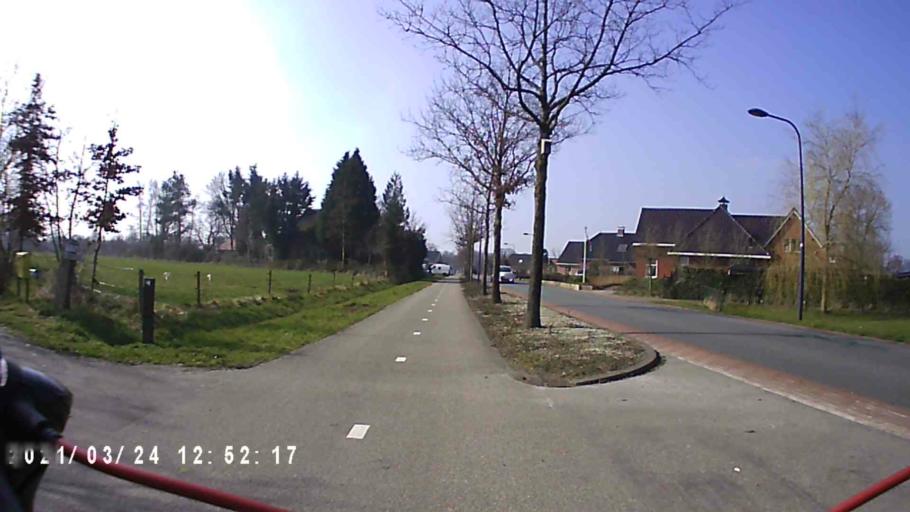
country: NL
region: Groningen
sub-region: Gemeente Leek
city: Leek
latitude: 53.1594
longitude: 6.3236
